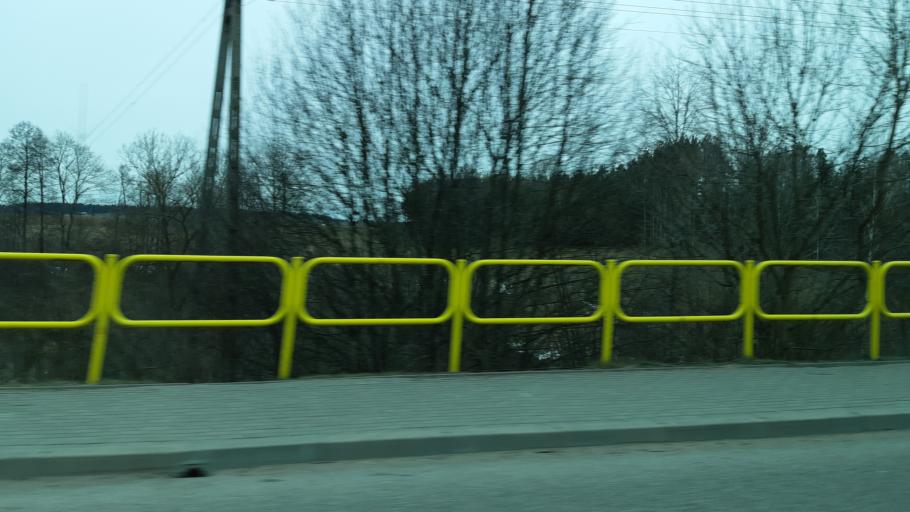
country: PL
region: Podlasie
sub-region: Suwalki
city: Suwalki
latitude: 54.3181
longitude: 22.9638
